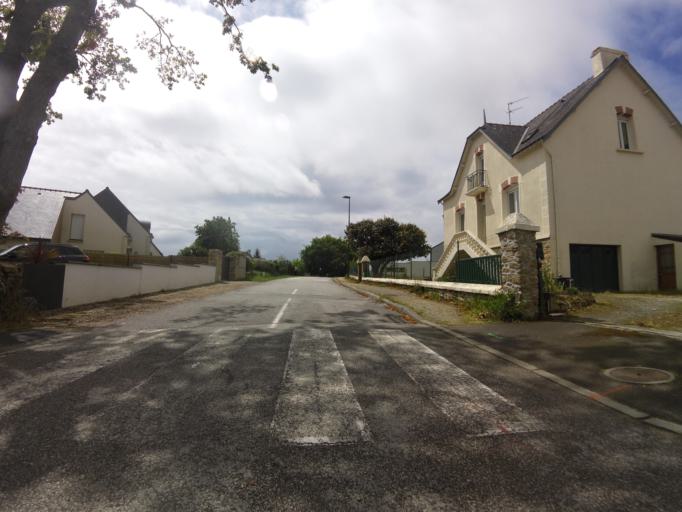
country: FR
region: Brittany
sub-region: Departement du Morbihan
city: Baden
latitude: 47.6131
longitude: -2.9213
